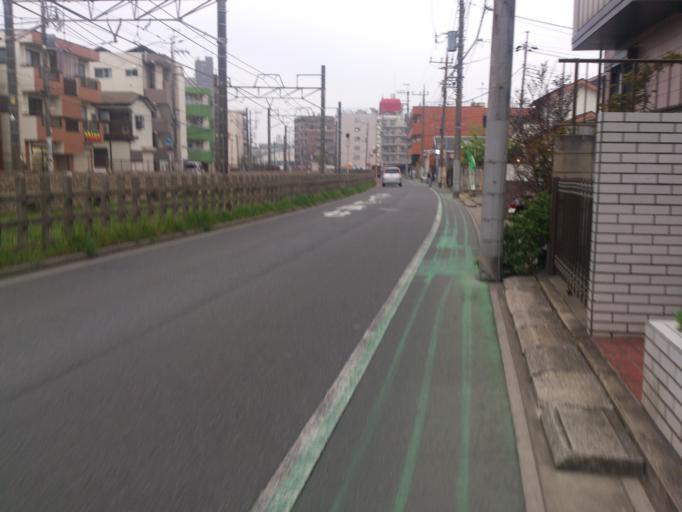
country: JP
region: Chiba
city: Kashiwa
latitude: 35.8043
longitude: 139.9542
